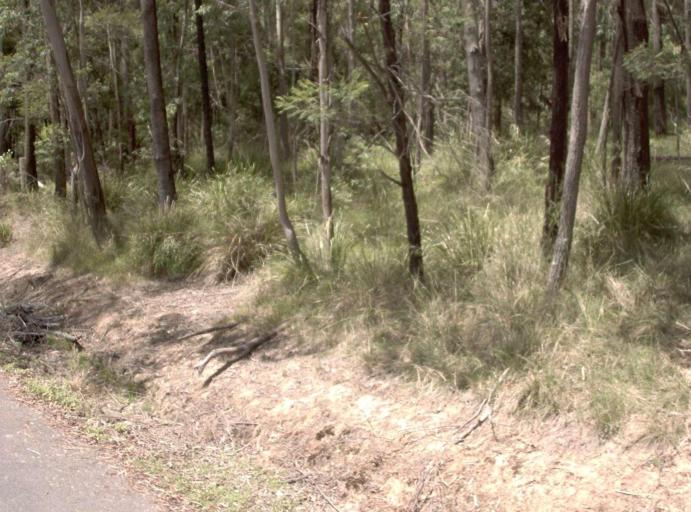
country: AU
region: New South Wales
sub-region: Bombala
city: Bombala
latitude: -37.4321
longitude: 149.0007
